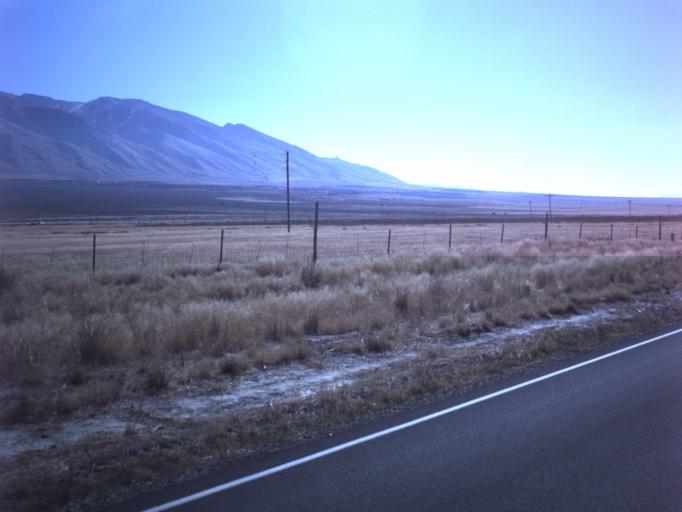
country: US
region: Utah
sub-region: Tooele County
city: Grantsville
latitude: 40.5064
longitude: -112.7480
